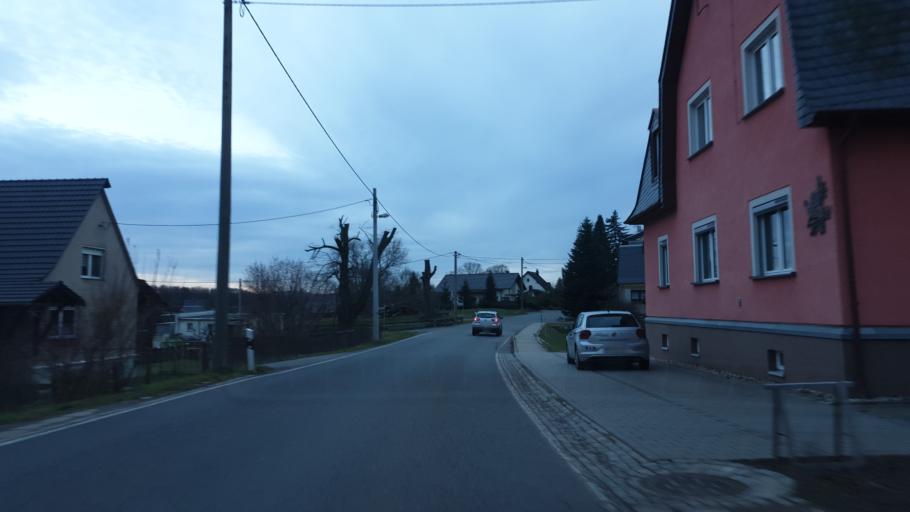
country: DE
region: Saxony
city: Hartenstein
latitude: 50.6801
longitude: 12.6685
